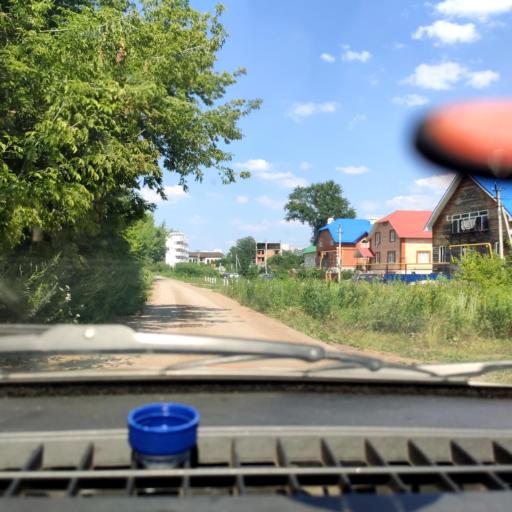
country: RU
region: Bashkortostan
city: Ufa
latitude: 54.6847
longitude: 55.9542
